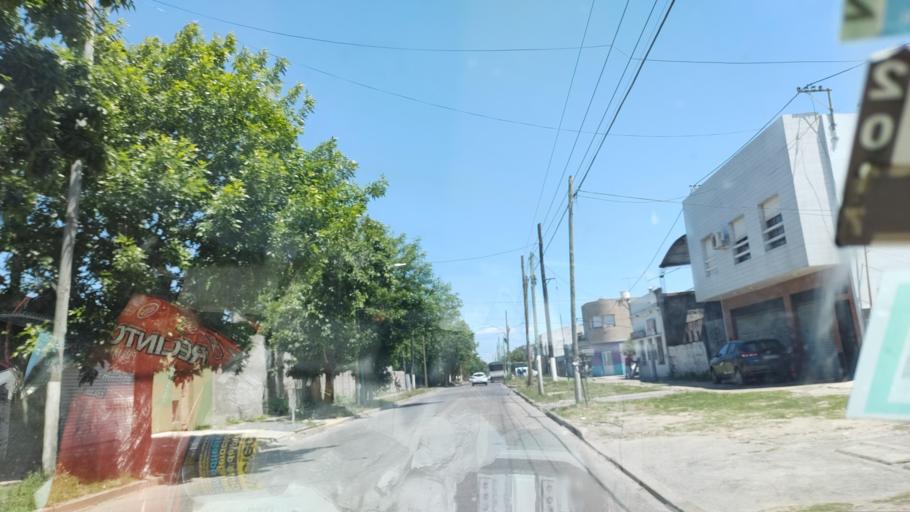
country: AR
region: Buenos Aires
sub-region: Partido de Berisso
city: Berisso
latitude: -34.8783
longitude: -57.8613
